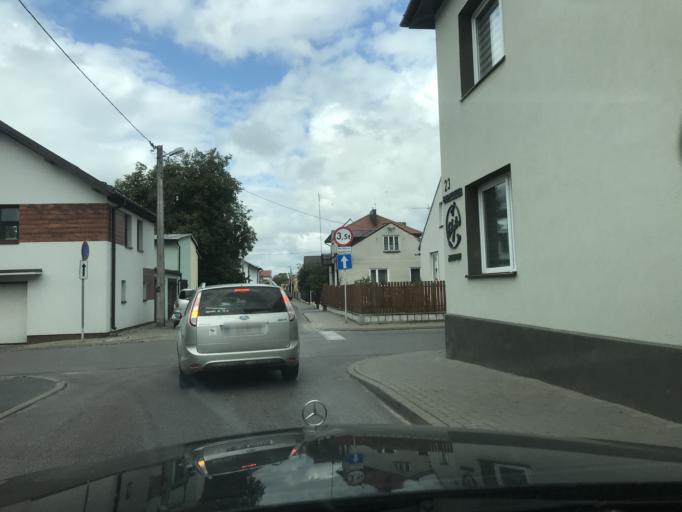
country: PL
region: Lublin Voivodeship
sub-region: Powiat janowski
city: Janow Lubelski
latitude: 50.7061
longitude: 22.4140
